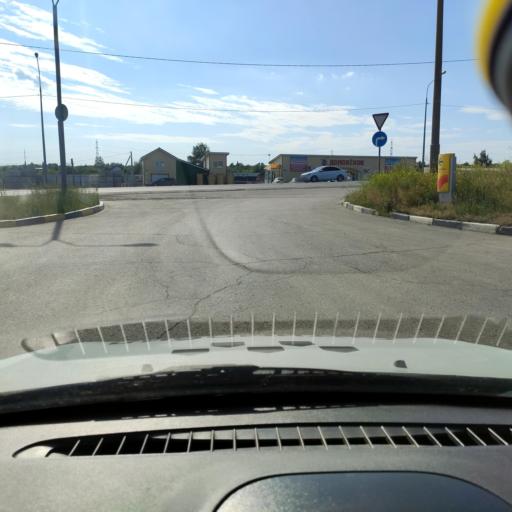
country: RU
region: Samara
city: Zhigulevsk
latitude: 53.3719
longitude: 49.4575
